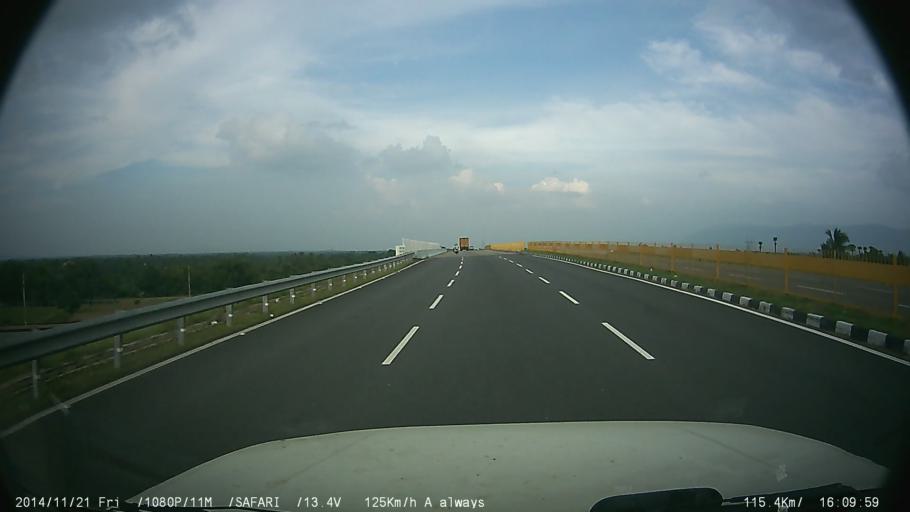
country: IN
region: Tamil Nadu
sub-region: Vellore
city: Jolarpettai
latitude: 12.5778
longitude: 78.4901
